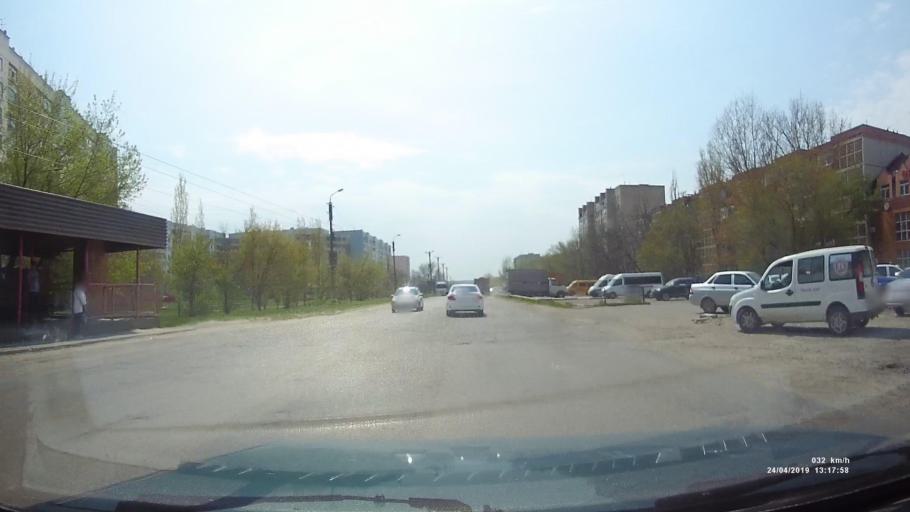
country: RU
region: Kalmykiya
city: Elista
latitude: 46.3044
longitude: 44.2971
